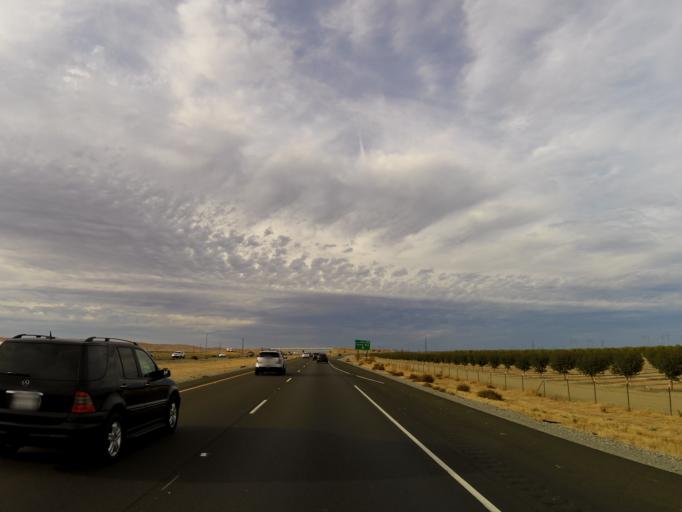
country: US
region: California
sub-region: Kings County
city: Kettleman City
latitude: 35.9304
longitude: -119.9075
